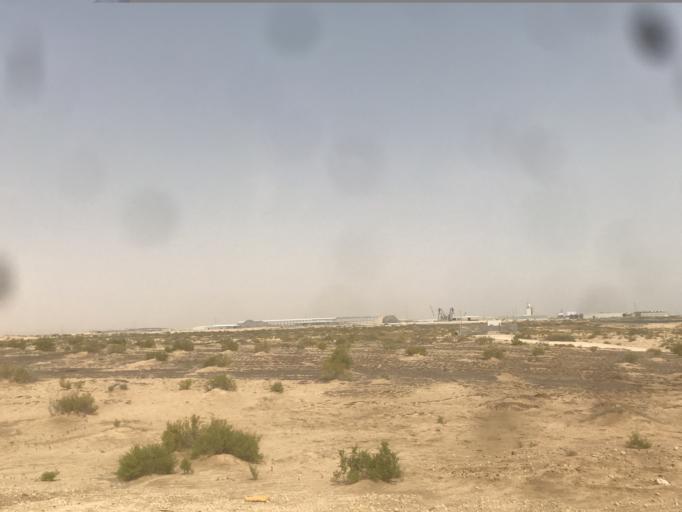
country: SA
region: Eastern Province
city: Abqaiq
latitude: 25.9103
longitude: 49.9462
